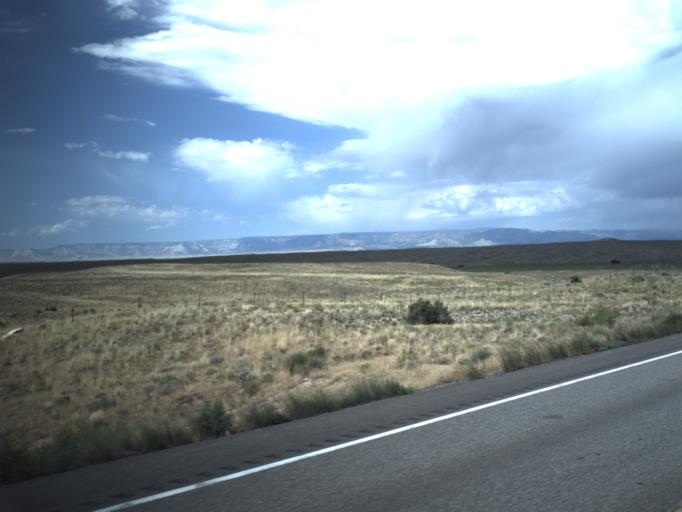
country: US
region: Utah
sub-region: Carbon County
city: East Carbon City
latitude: 39.5188
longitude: -110.5572
